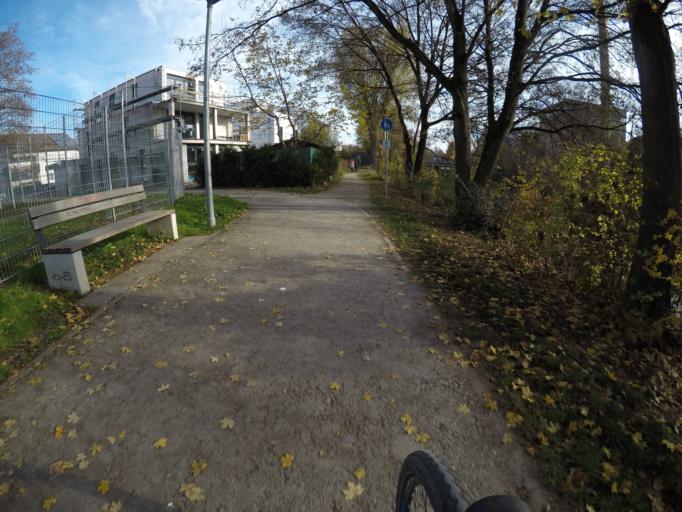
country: DE
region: Baden-Wuerttemberg
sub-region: Regierungsbezirk Stuttgart
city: Weinstadt-Endersbach
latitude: 48.8171
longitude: 9.3670
